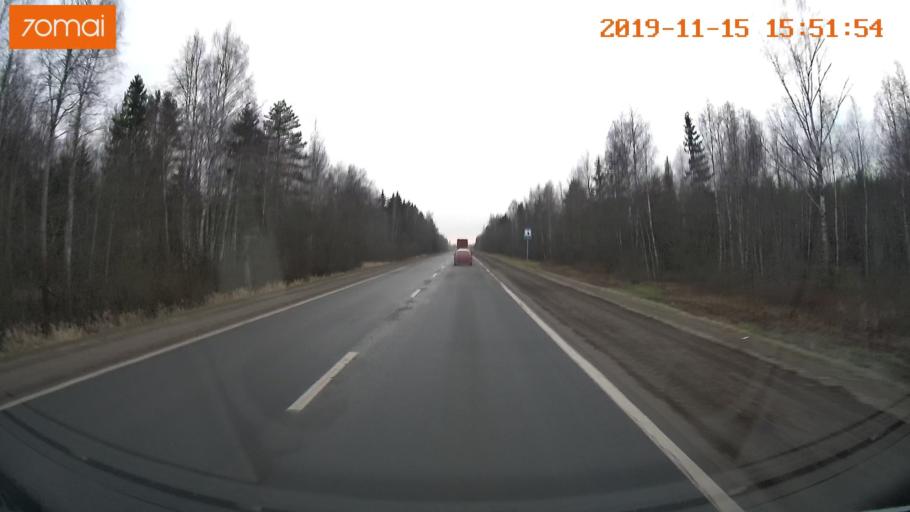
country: RU
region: Jaroslavl
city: Yaroslavl
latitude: 57.8892
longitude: 40.0039
